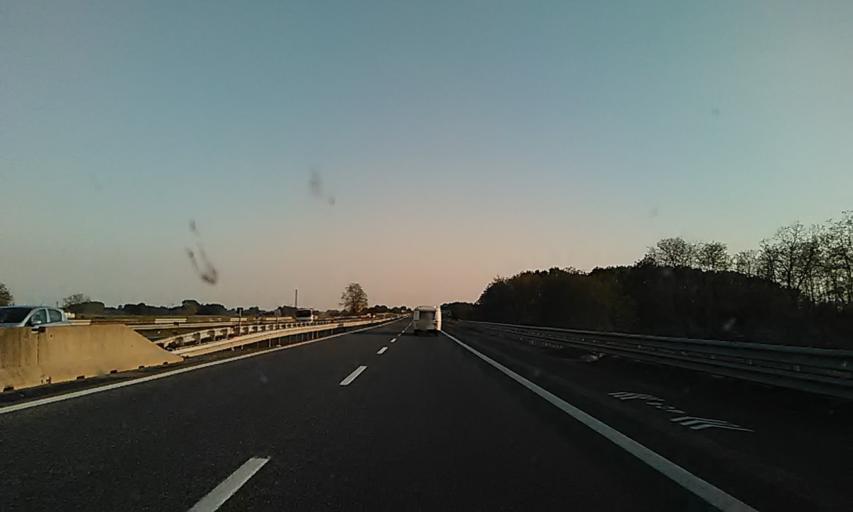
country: IT
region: Piedmont
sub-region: Provincia di Novara
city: Sillavengo
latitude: 45.5245
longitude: 8.4319
